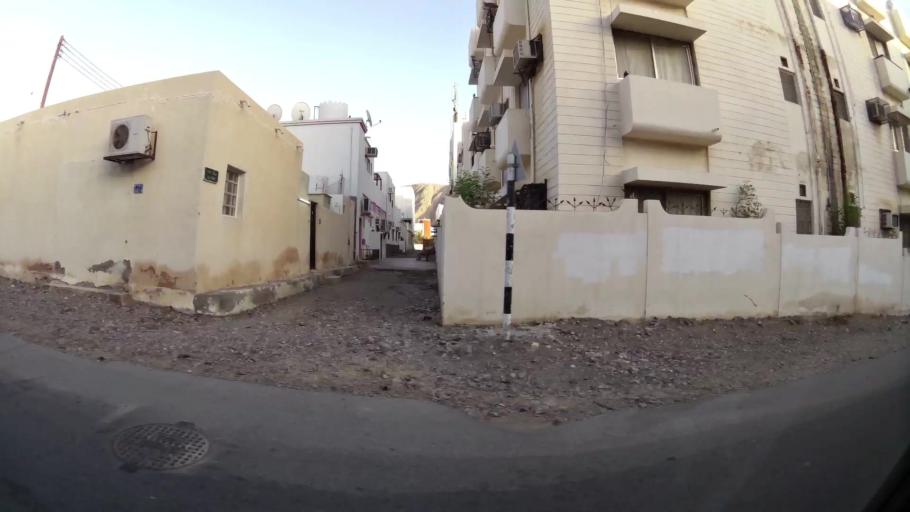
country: OM
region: Muhafazat Masqat
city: Muscat
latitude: 23.5746
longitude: 58.5715
